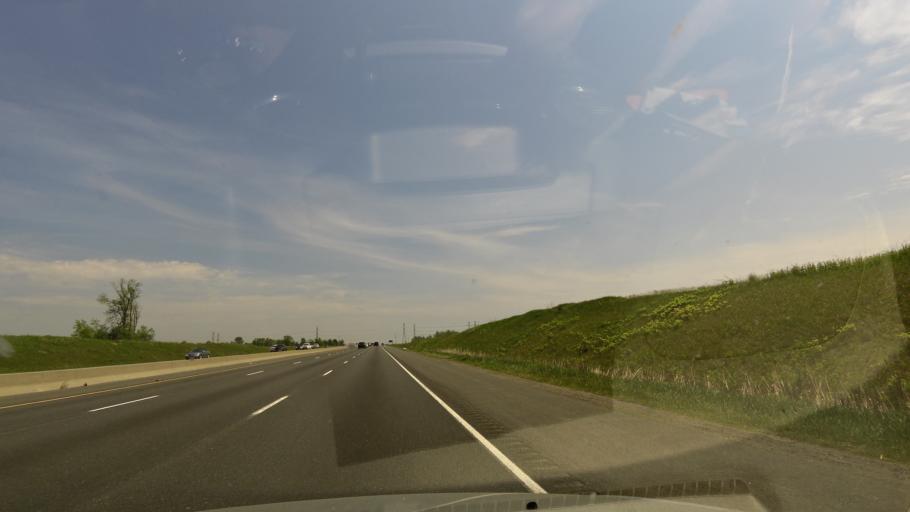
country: CA
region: Ontario
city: Oshawa
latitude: 43.8814
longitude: -78.7421
